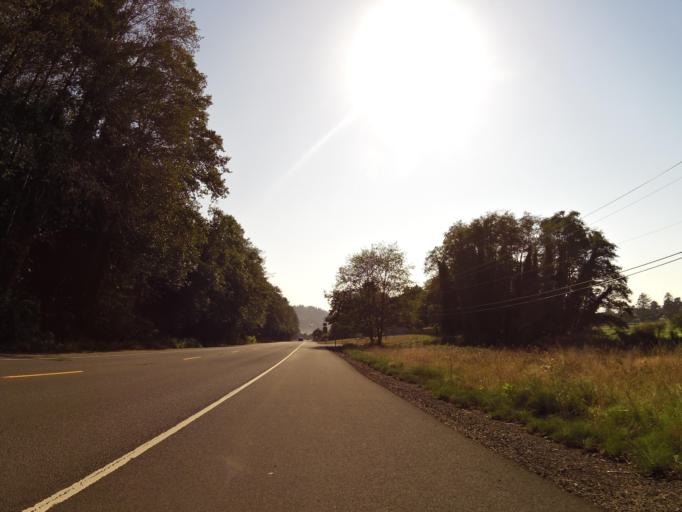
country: US
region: Oregon
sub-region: Tillamook County
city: Pacific City
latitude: 45.1085
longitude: -123.9758
